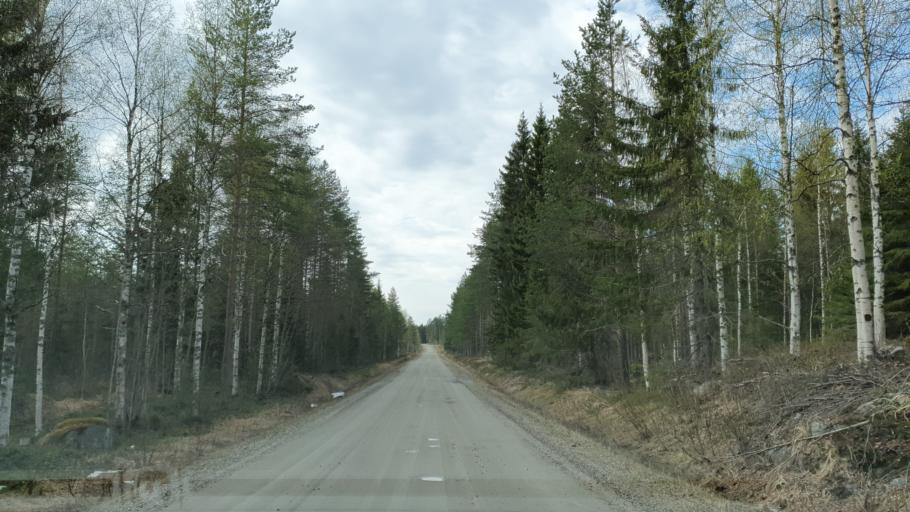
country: FI
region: Kainuu
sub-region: Kehys-Kainuu
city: Kuhmo
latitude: 64.0958
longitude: 29.9065
